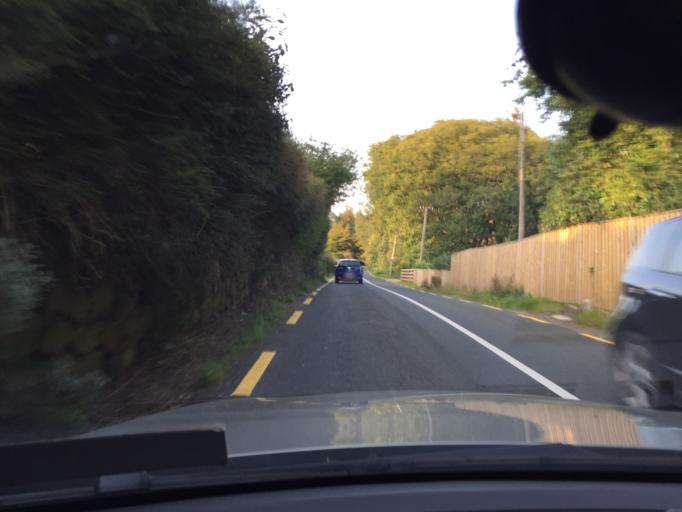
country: IE
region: Leinster
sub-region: Wicklow
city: Rathdrum
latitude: 53.0177
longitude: -6.2754
